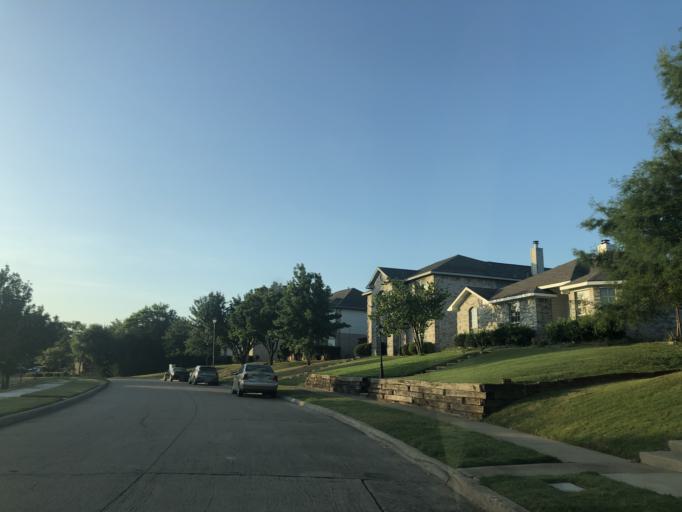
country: US
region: Texas
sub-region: Dallas County
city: Duncanville
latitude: 32.6477
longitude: -96.9537
